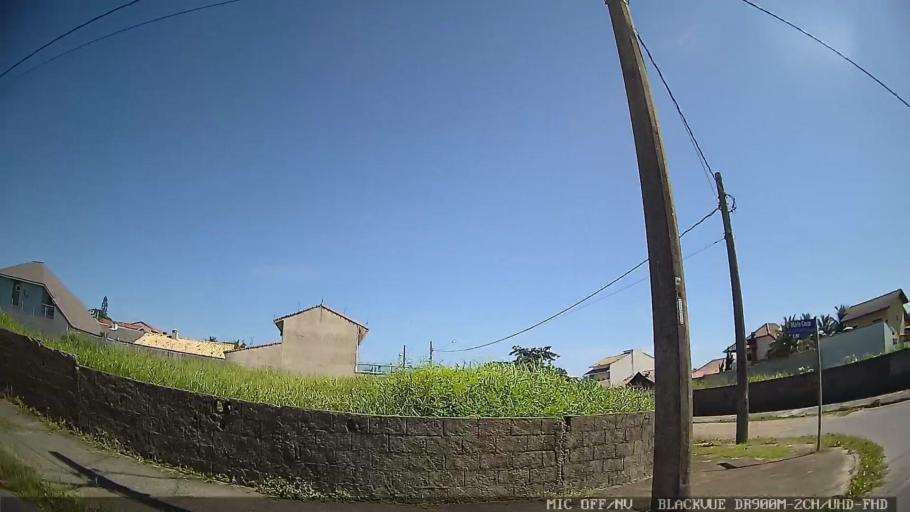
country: BR
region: Sao Paulo
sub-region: Peruibe
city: Peruibe
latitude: -24.2883
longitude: -46.9531
